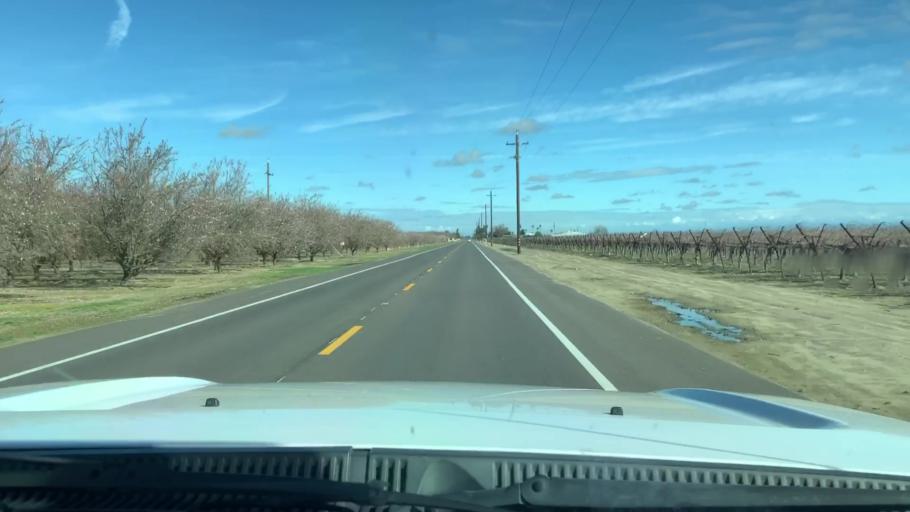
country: US
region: California
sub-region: Fresno County
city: Laton
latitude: 36.5201
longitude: -119.6829
